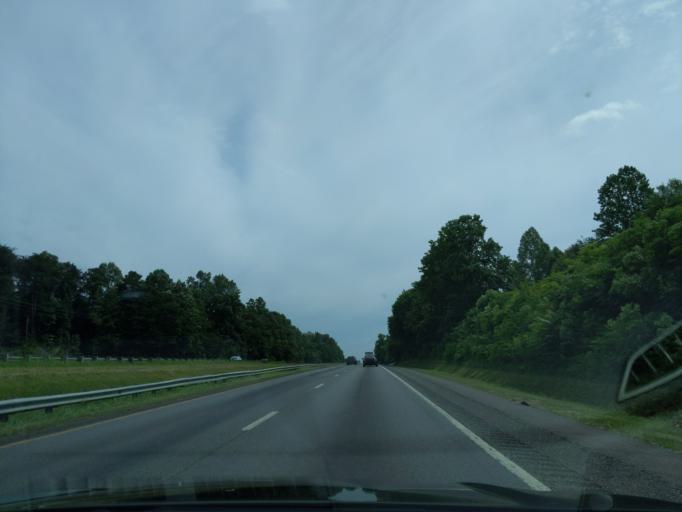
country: US
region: North Carolina
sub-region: Cleveland County
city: Kings Mountain
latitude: 35.2149
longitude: -81.3474
